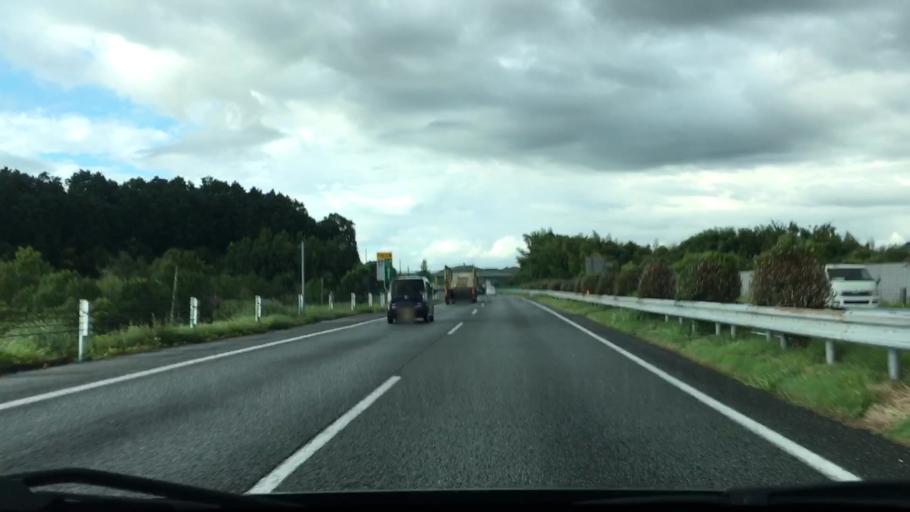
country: JP
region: Fukuoka
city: Koga
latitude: 33.7088
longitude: 130.4875
